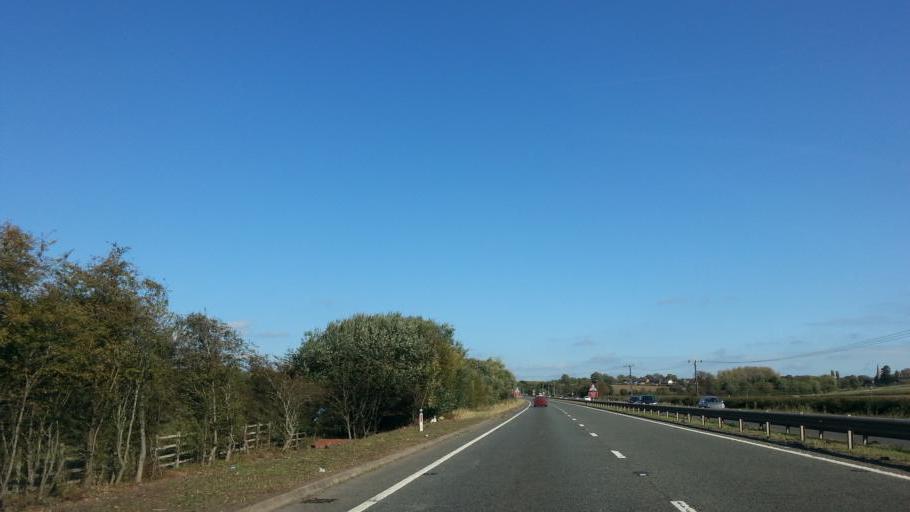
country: GB
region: England
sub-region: Northamptonshire
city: Stanwick
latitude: 52.3268
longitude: -0.5825
